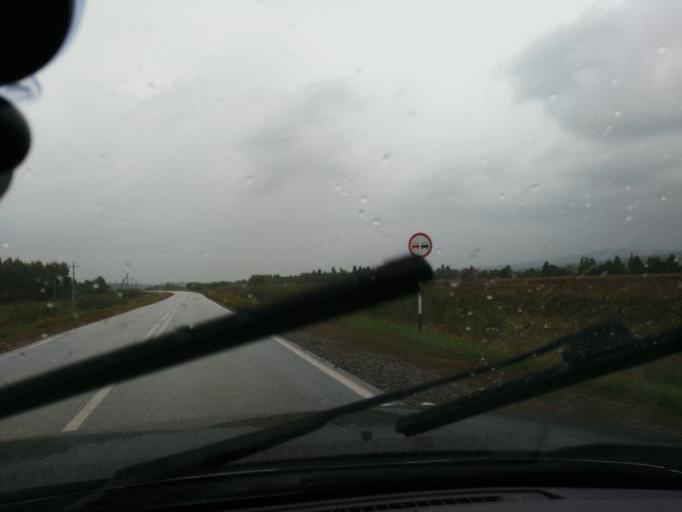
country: RU
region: Perm
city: Barda
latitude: 57.0784
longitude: 55.5428
